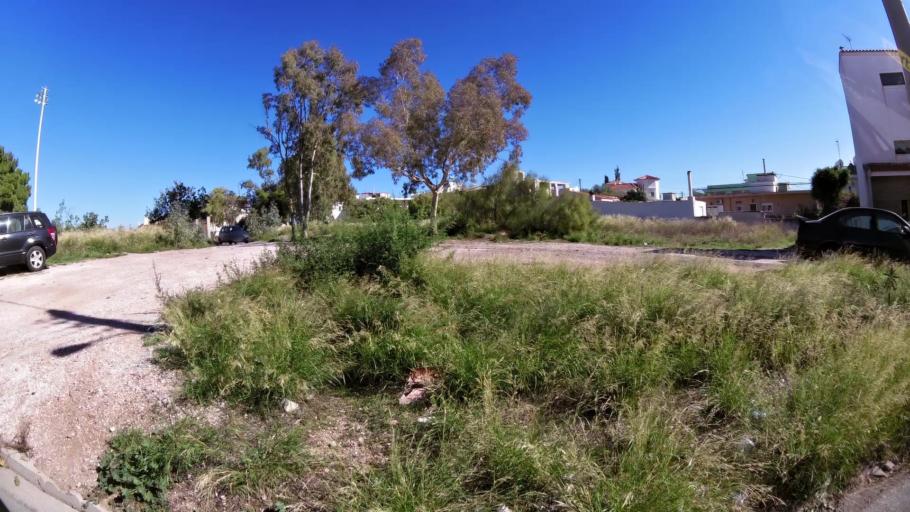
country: GR
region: Attica
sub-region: Nomarchia Anatolikis Attikis
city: Koropi
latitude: 37.9006
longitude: 23.8803
